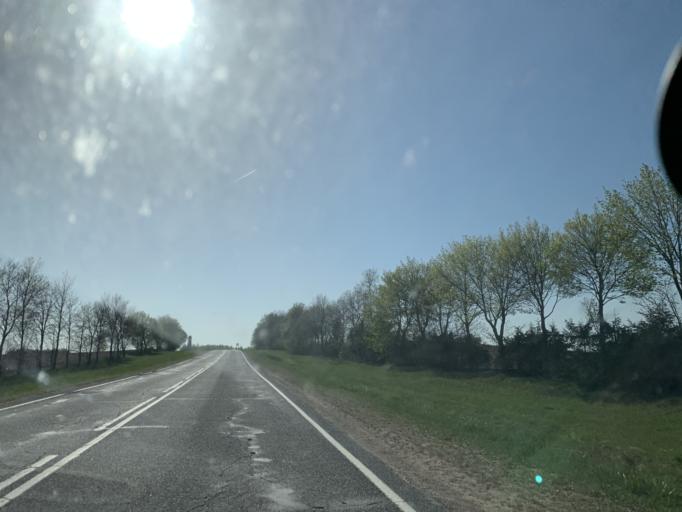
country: BY
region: Minsk
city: Nyasvizh
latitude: 53.2472
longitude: 26.8820
